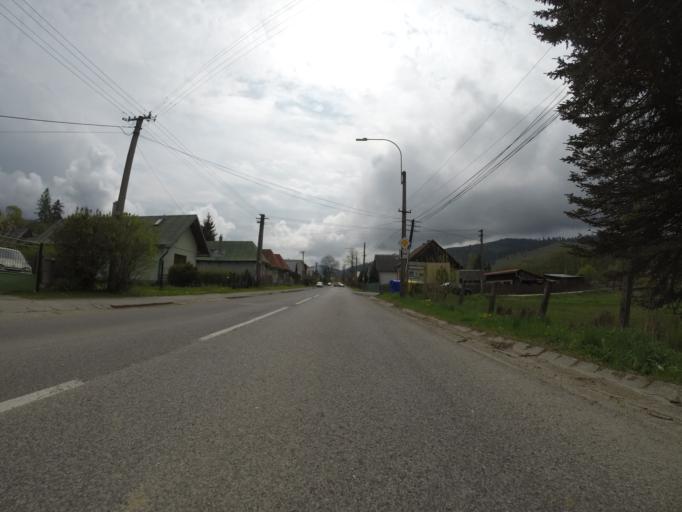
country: SK
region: Banskobystricky
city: Cierny Balog
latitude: 48.7652
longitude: 19.7724
